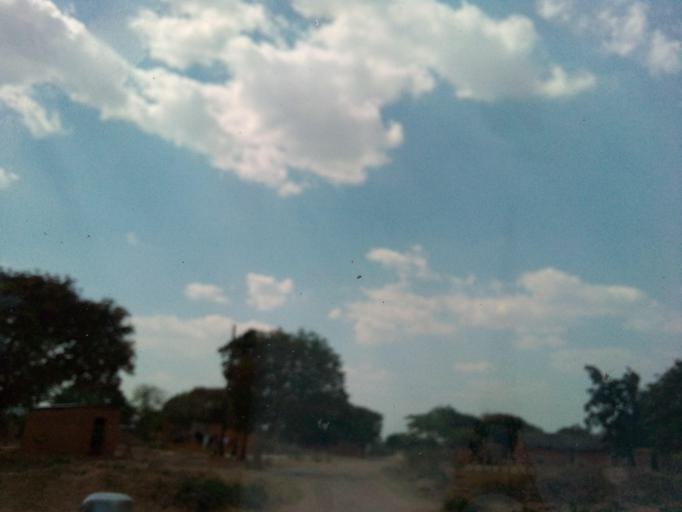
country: ZM
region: Northern
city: Mpika
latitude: -11.8336
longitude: 31.3879
